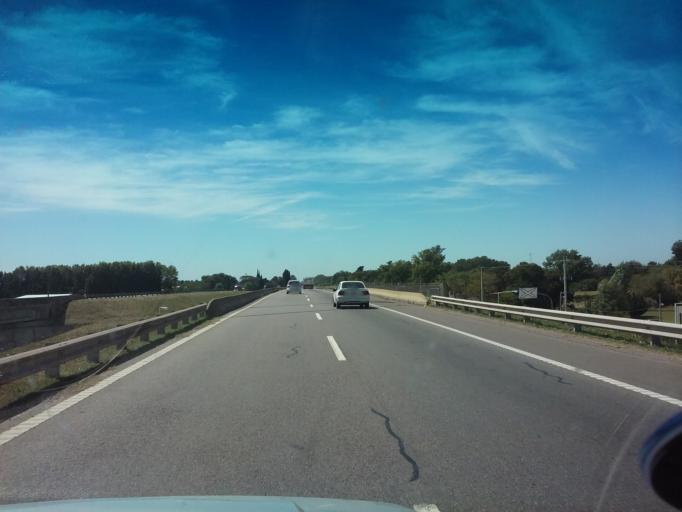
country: AR
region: Buenos Aires
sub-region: Partido de Mercedes
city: Mercedes
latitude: -34.6616
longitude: -59.3825
